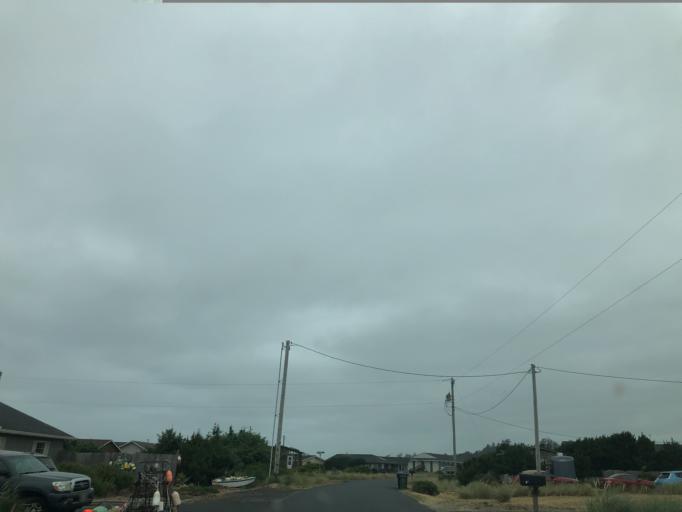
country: US
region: Oregon
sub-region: Lincoln County
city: Waldport
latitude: 44.4290
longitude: -124.0801
